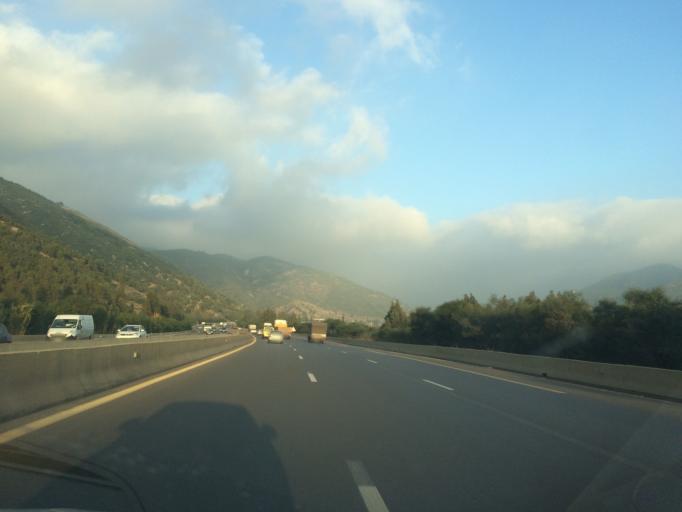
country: DZ
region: Tipaza
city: Hadjout
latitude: 36.3847
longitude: 2.4896
